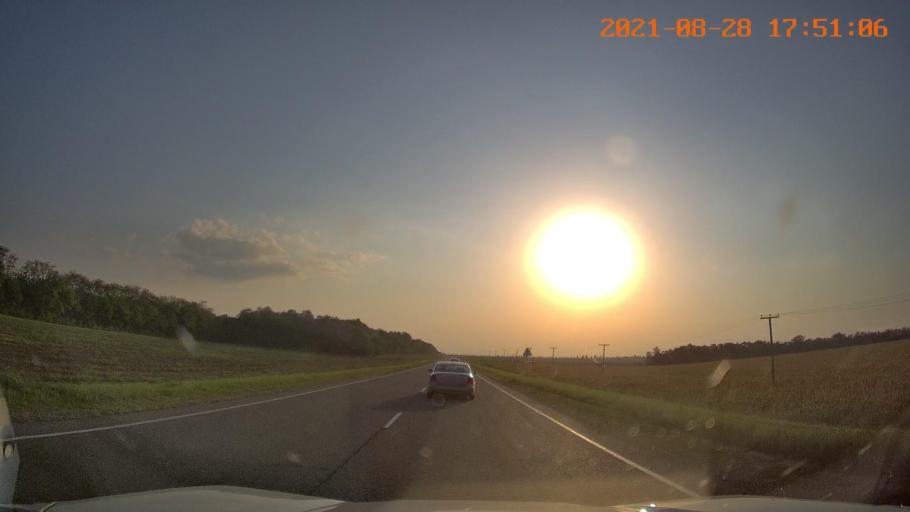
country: RU
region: Krasnodarskiy
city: Konstantinovskaya
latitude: 44.9451
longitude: 40.8021
